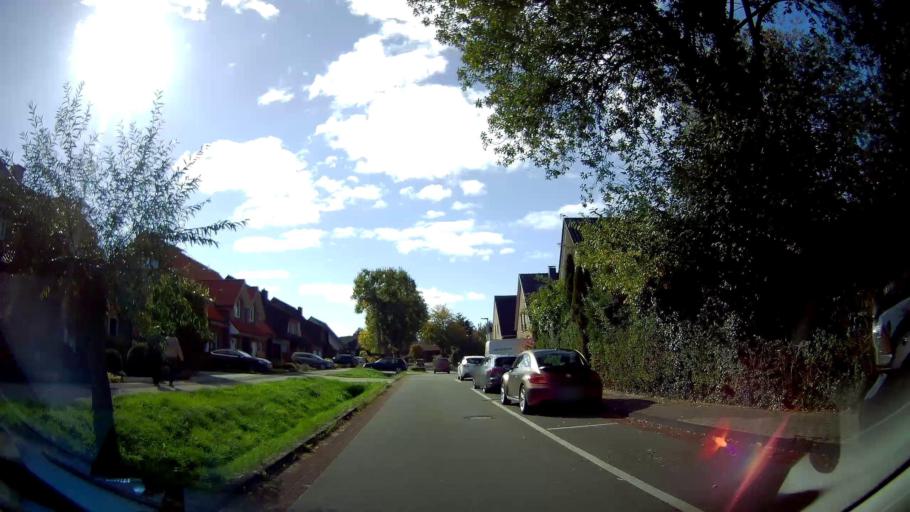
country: DE
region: North Rhine-Westphalia
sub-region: Regierungsbezirk Dusseldorf
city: Hunxe
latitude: 51.6355
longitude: 6.7678
